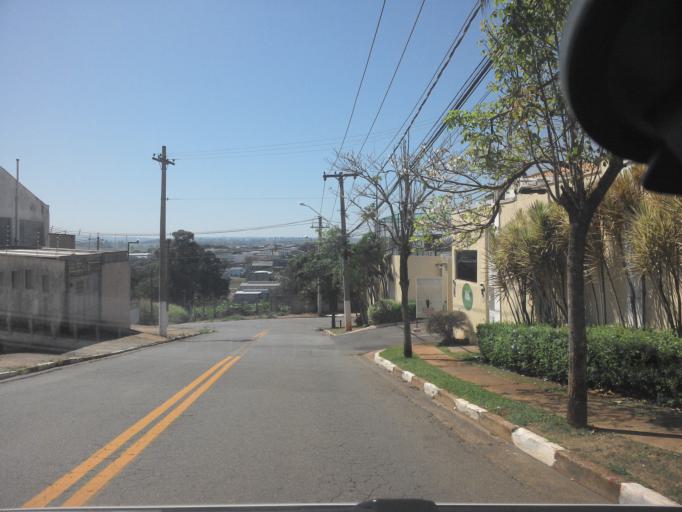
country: BR
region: Sao Paulo
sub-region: Campinas
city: Campinas
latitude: -22.8462
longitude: -47.0499
